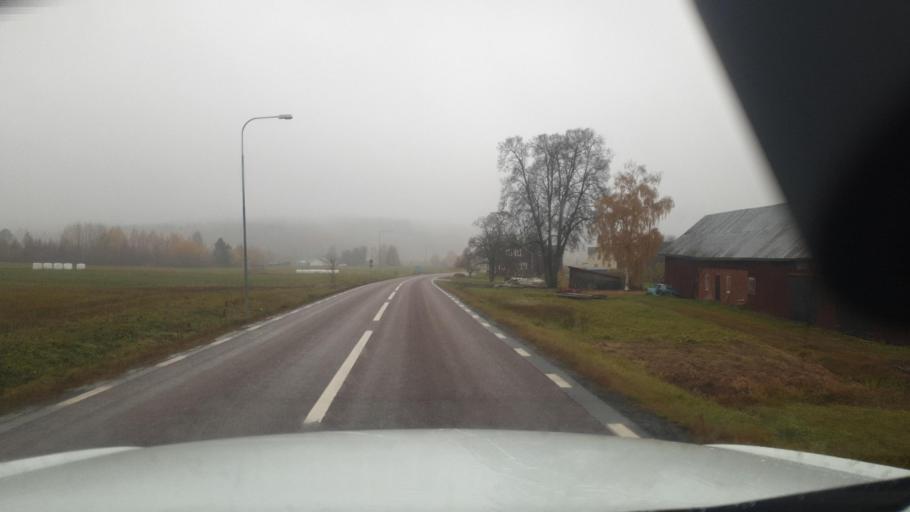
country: SE
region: Vaermland
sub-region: Sunne Kommun
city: Sunne
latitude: 59.8469
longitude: 12.9460
